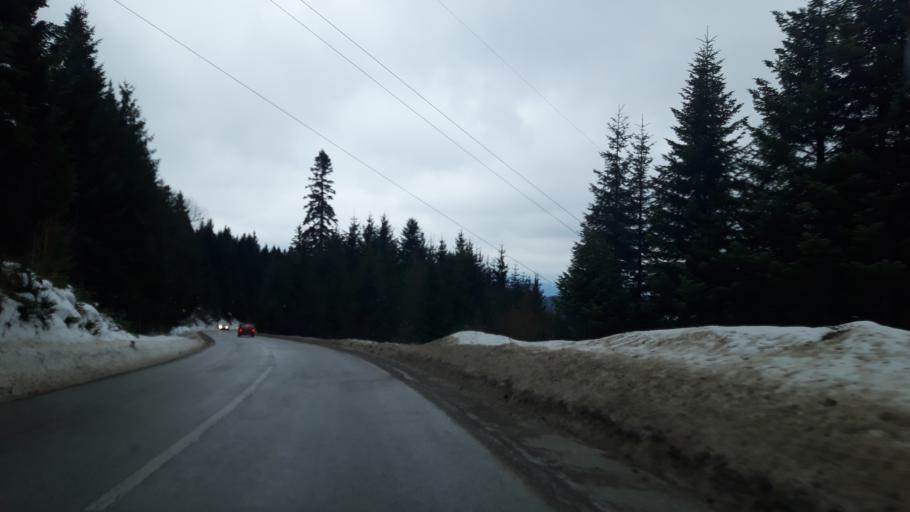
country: BA
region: Republika Srpska
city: Pale
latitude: 43.9147
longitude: 18.6464
